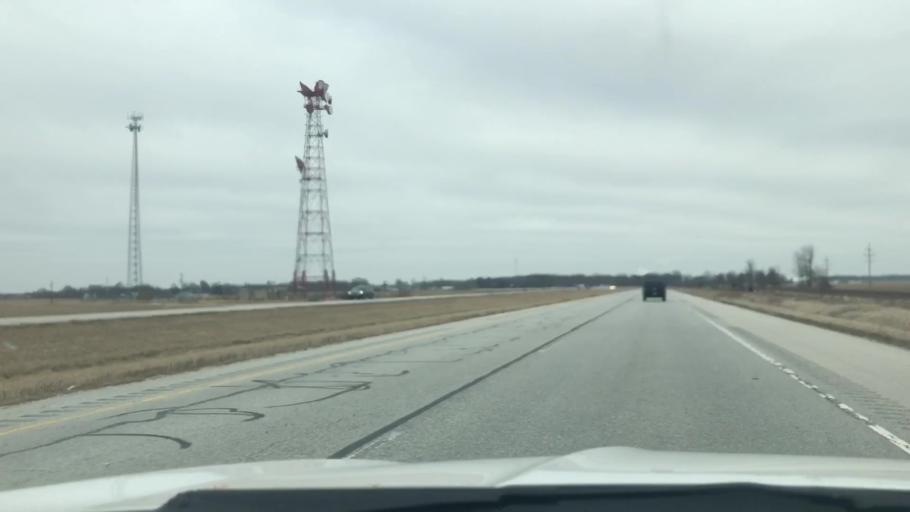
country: US
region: Indiana
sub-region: Cass County
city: Georgetown
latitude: 40.6673
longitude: -86.5261
